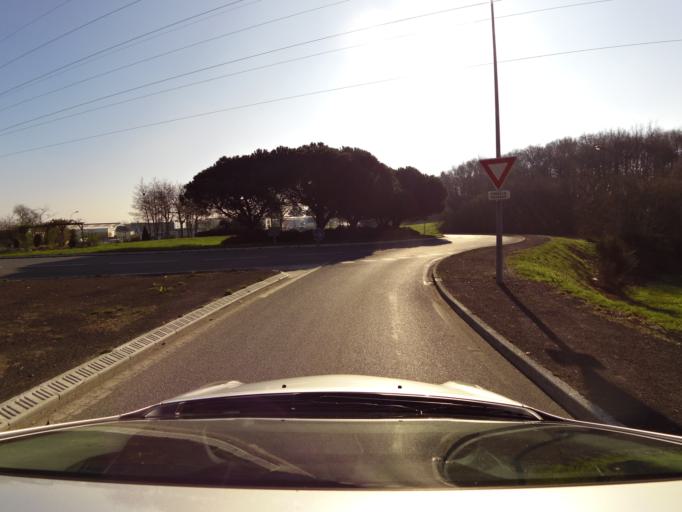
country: FR
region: Brittany
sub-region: Departement du Morbihan
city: Gestel
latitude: 47.8067
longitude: -3.4651
